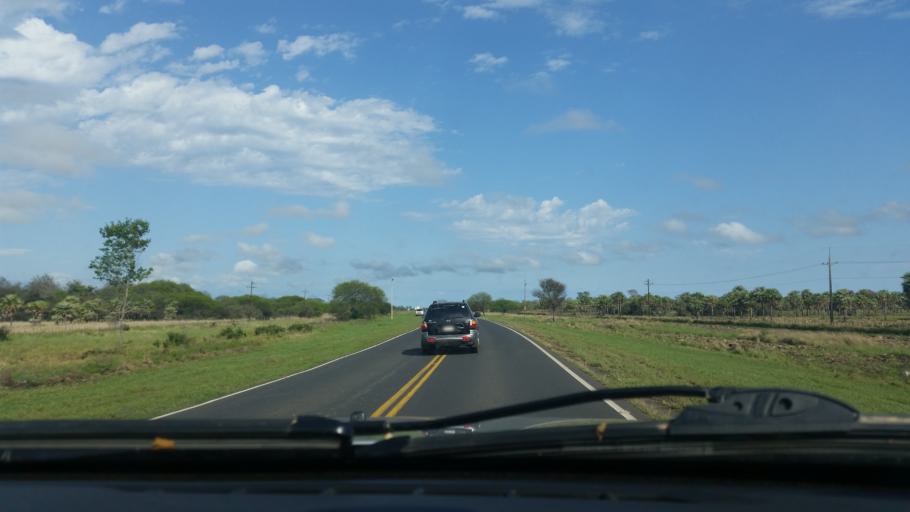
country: PY
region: Presidente Hayes
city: Benjamin Aceval
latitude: -24.9222
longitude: -57.5766
